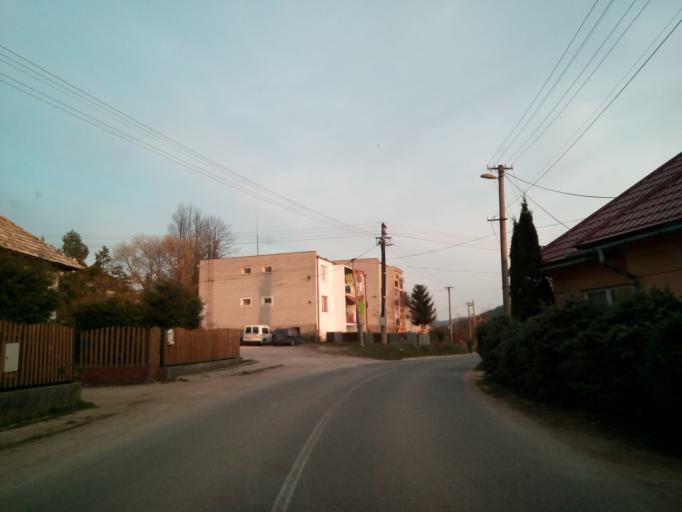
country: SK
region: Kosicky
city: Dobsina
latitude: 48.7111
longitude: 20.2872
